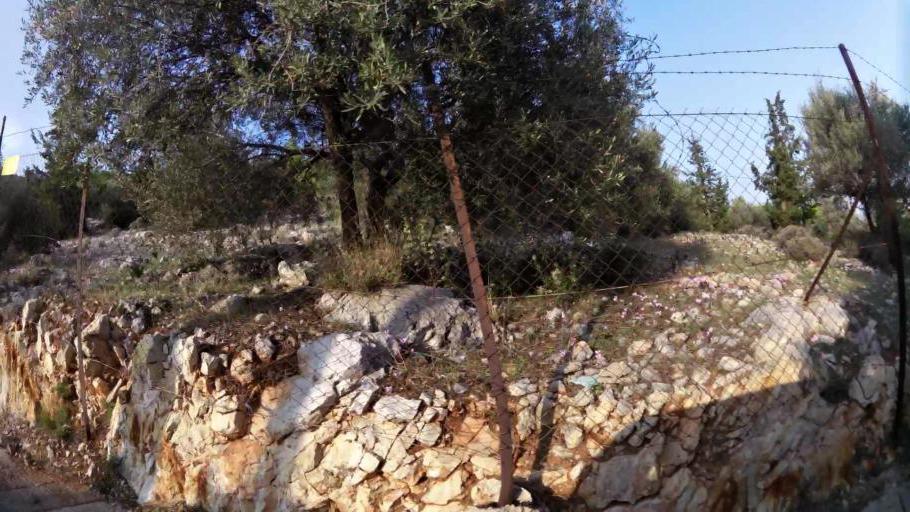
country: GR
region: Attica
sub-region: Nomarchia Athinas
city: Petroupolis
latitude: 38.0492
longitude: 23.6782
